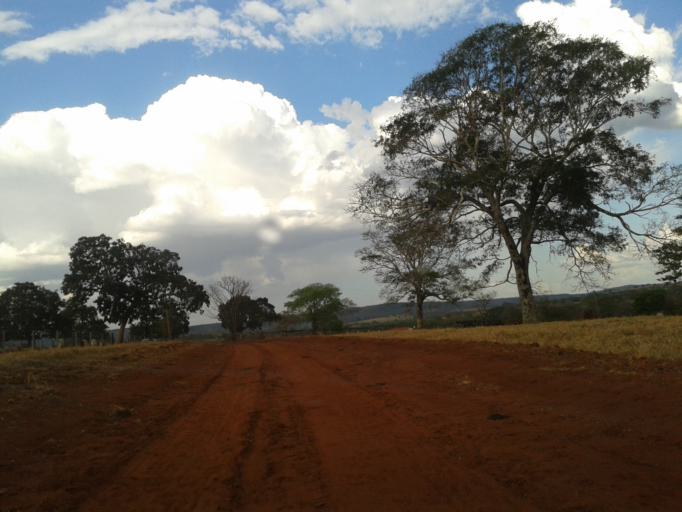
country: BR
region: Minas Gerais
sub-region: Santa Vitoria
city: Santa Vitoria
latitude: -19.1710
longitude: -49.9628
